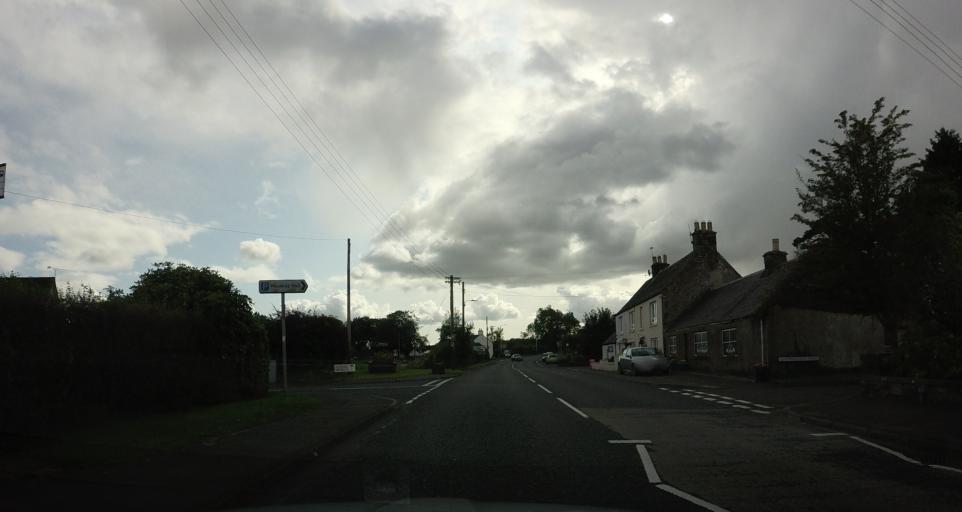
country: GB
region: Scotland
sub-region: Fife
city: Saline
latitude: 56.1656
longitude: -3.5798
